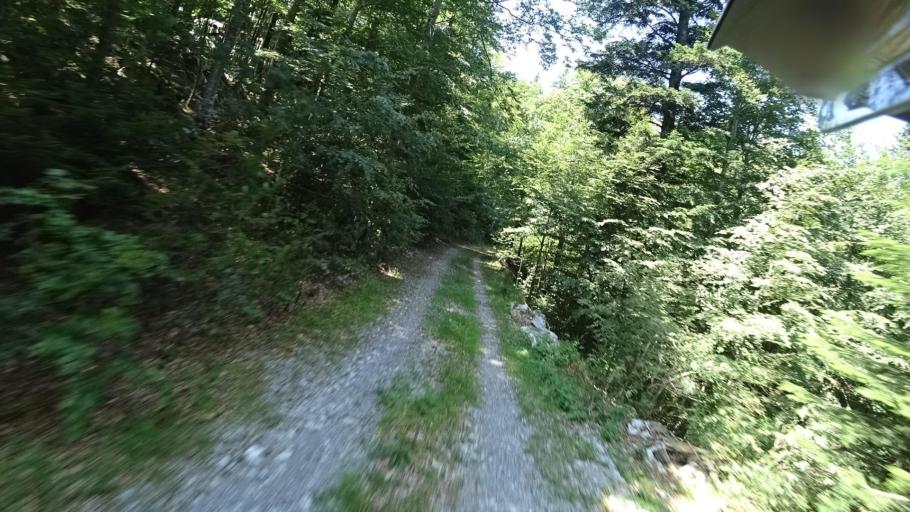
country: HR
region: Primorsko-Goranska
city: Bribir
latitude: 45.2636
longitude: 14.8603
